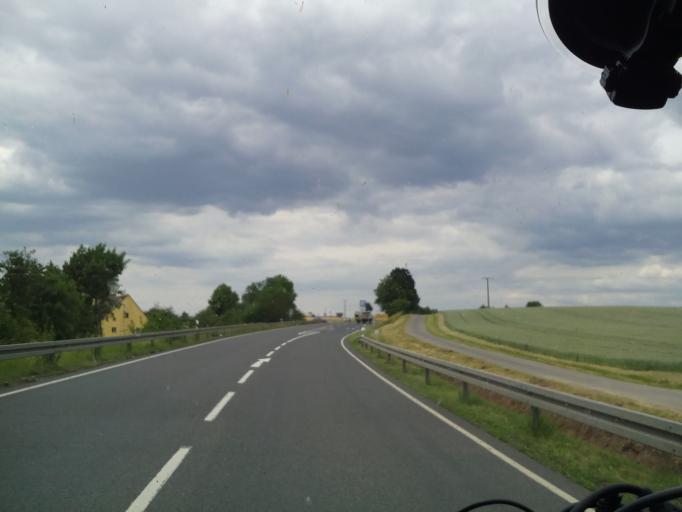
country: DE
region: Bavaria
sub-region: Regierungsbezirk Unterfranken
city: Untermerzbach
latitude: 50.1187
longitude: 10.8720
